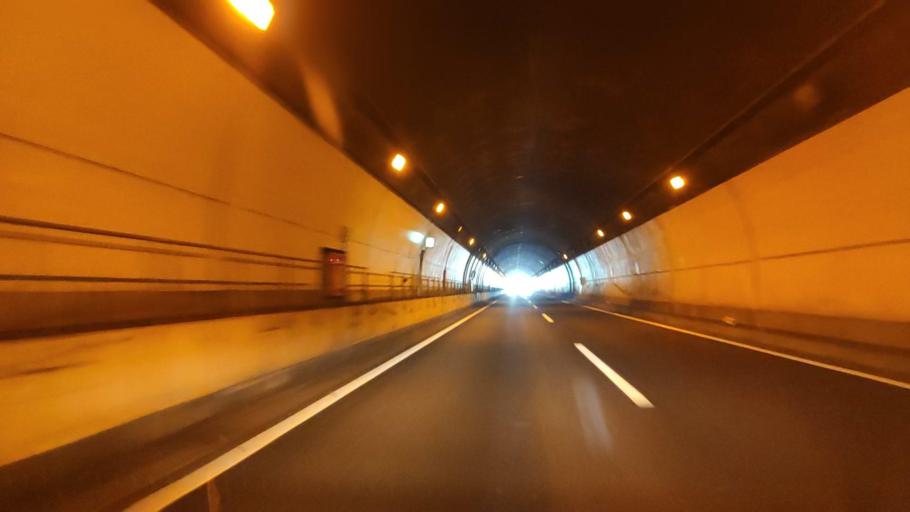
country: JP
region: Akita
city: Hanawa
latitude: 40.0170
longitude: 140.9856
